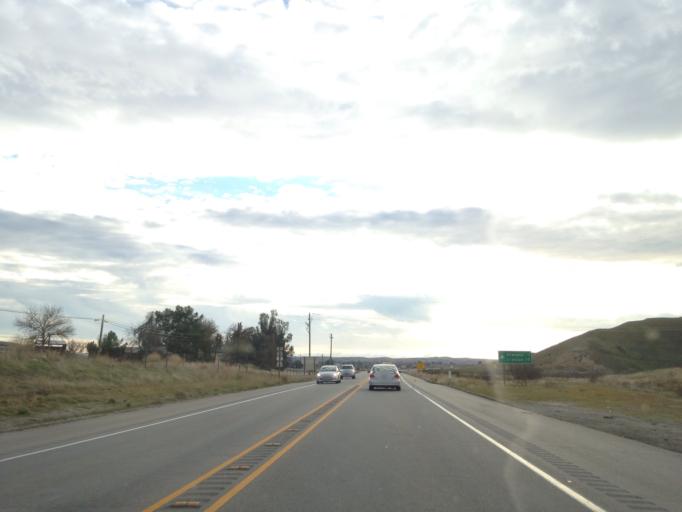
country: US
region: California
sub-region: San Luis Obispo County
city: Shandon
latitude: 35.6683
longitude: -120.3577
